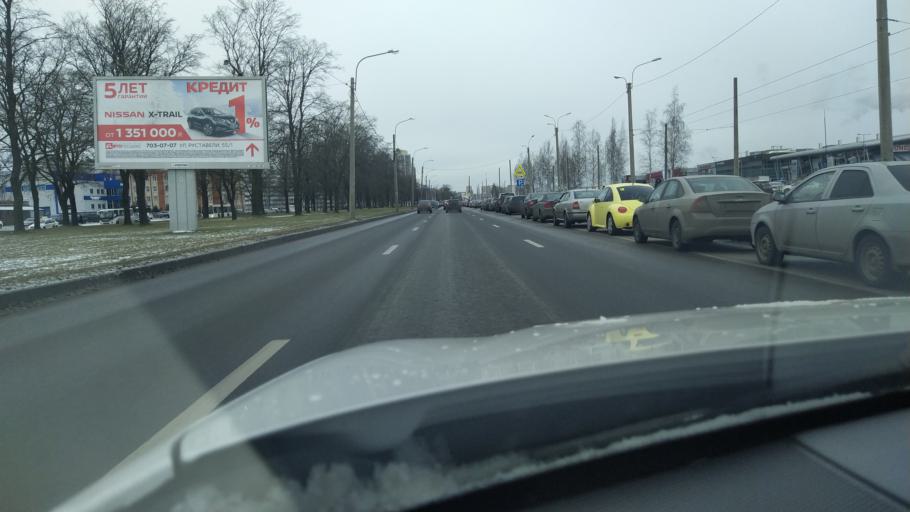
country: RU
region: St.-Petersburg
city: Grazhdanka
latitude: 60.0228
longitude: 30.4323
